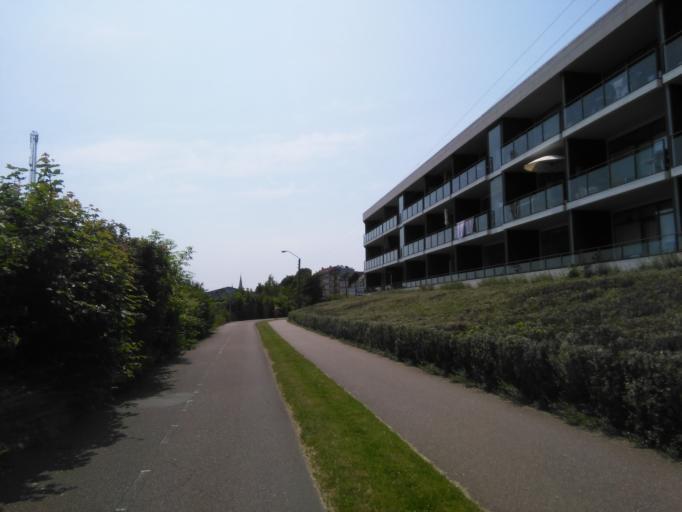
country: DK
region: Central Jutland
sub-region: Arhus Kommune
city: Arhus
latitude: 56.1679
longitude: 10.2207
